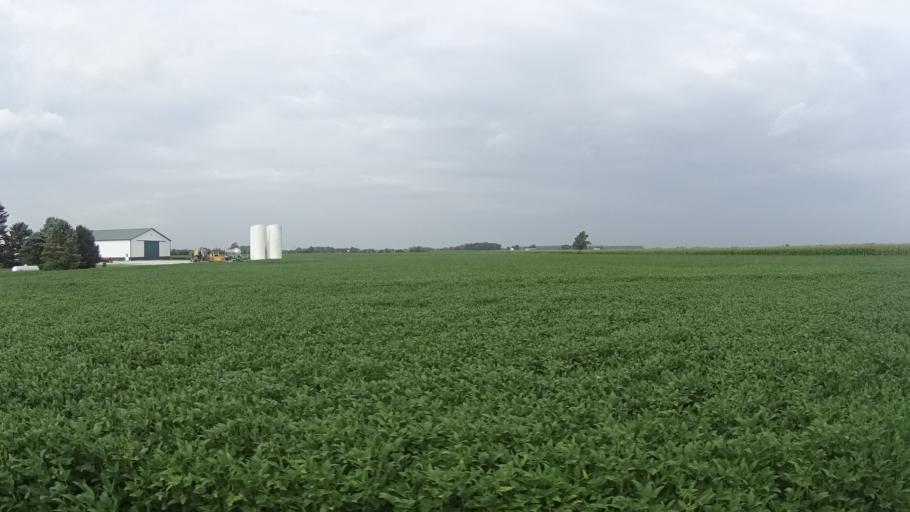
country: US
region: Indiana
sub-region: Madison County
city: Lapel
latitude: 40.0303
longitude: -85.8055
